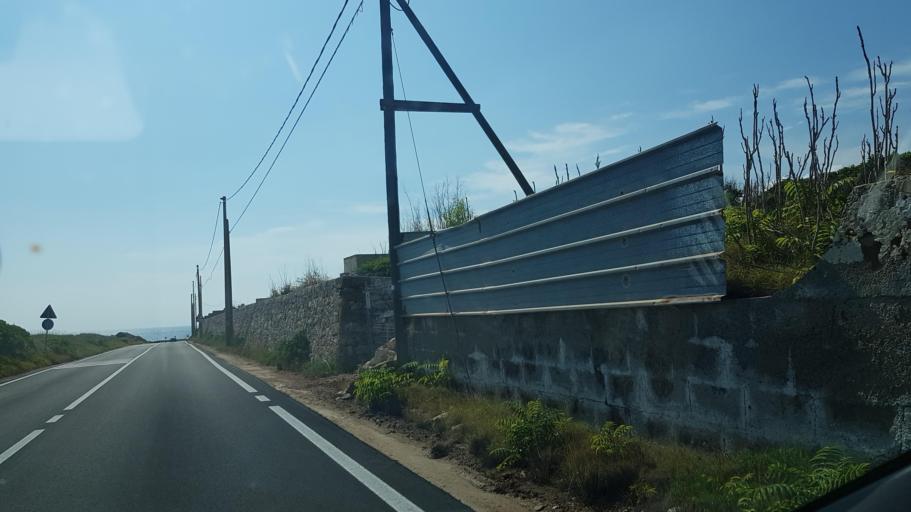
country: IT
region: Apulia
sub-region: Provincia di Lecce
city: Leuca
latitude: 39.7962
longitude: 18.3392
